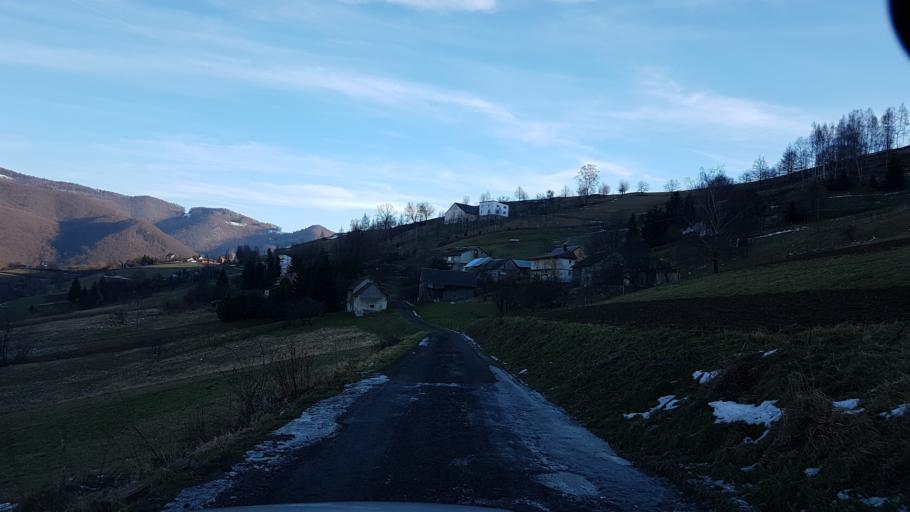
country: PL
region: Lesser Poland Voivodeship
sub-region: Powiat nowosadecki
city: Rytro
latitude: 49.4969
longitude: 20.6635
